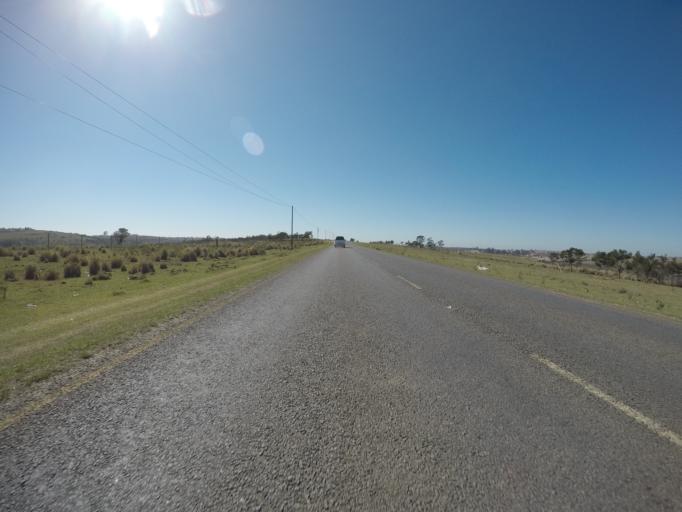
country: ZA
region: Eastern Cape
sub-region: OR Tambo District Municipality
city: Mthatha
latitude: -31.8010
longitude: 28.7483
